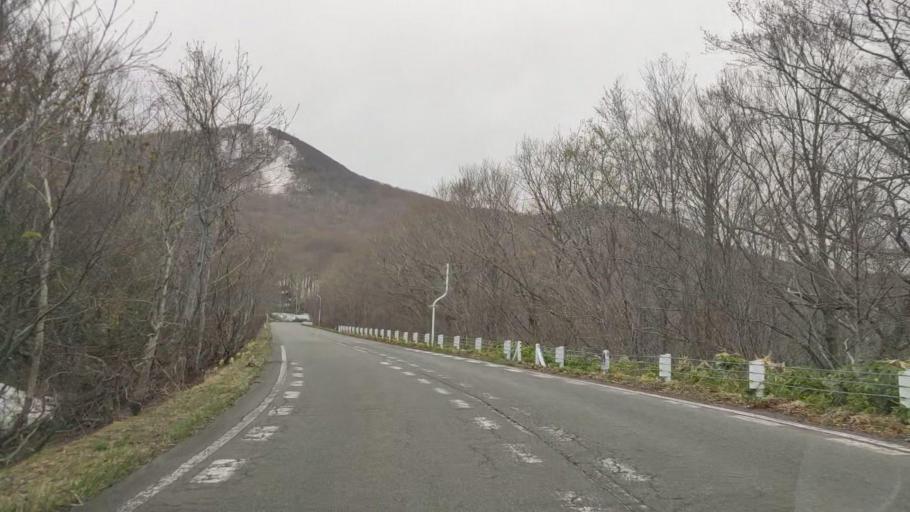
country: JP
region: Aomori
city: Aomori Shi
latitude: 40.6560
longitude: 140.9552
